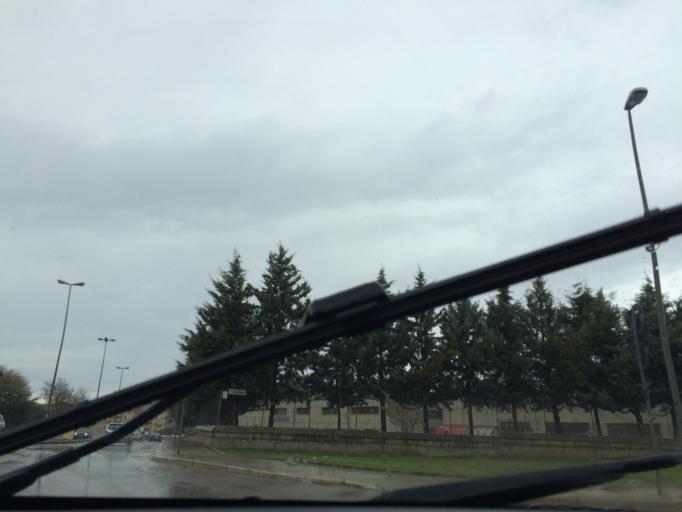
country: IT
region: Basilicate
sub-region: Provincia di Matera
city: Matera
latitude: 40.6791
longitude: 16.5806
